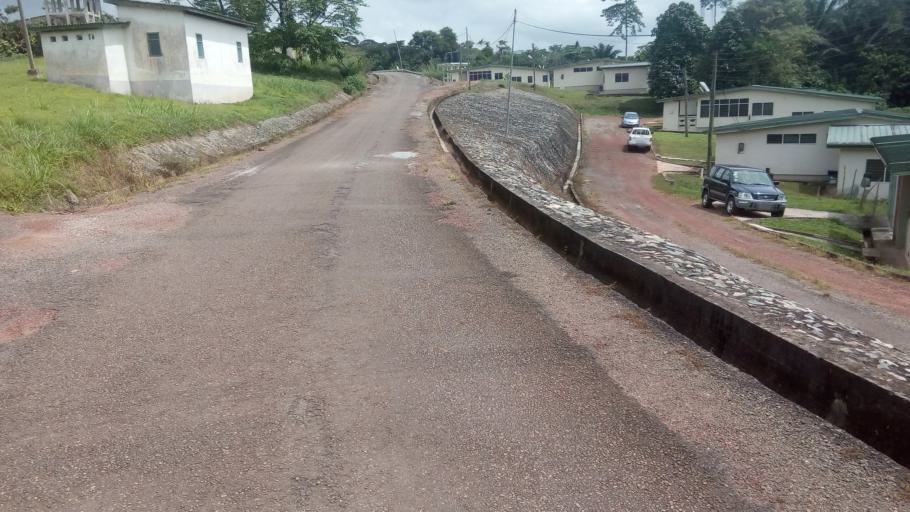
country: GH
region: Western
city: Tarkwa
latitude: 5.2939
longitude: -2.0094
